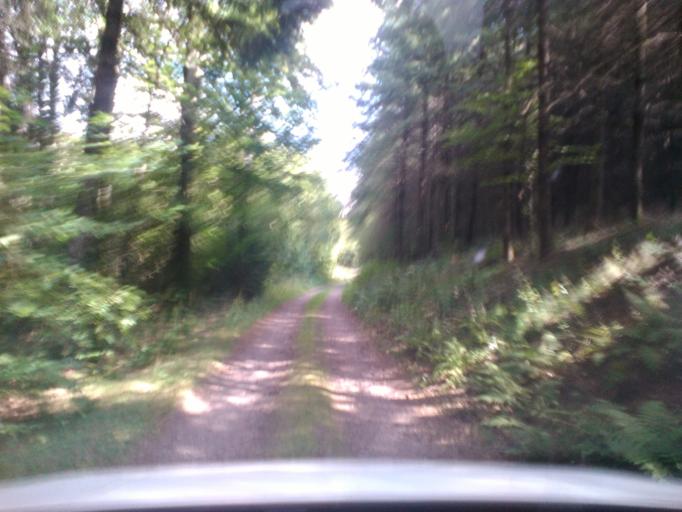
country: FR
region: Lorraine
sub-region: Departement des Vosges
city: Senones
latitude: 48.3518
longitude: 7.0477
